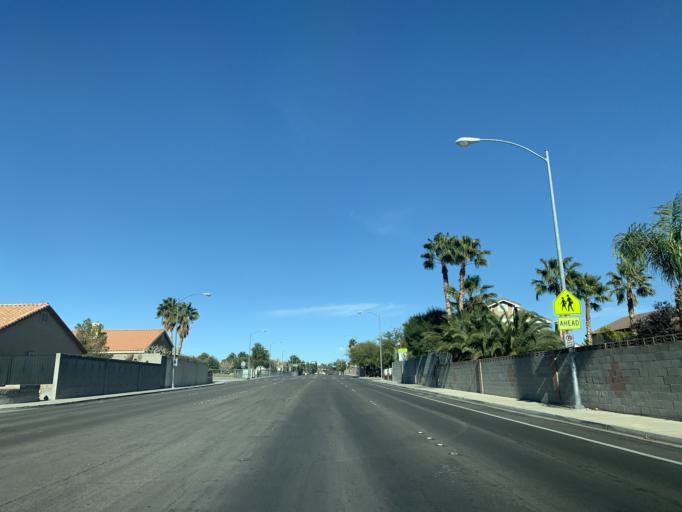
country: US
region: Nevada
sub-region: Clark County
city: Summerlin South
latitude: 36.1233
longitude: -115.2879
